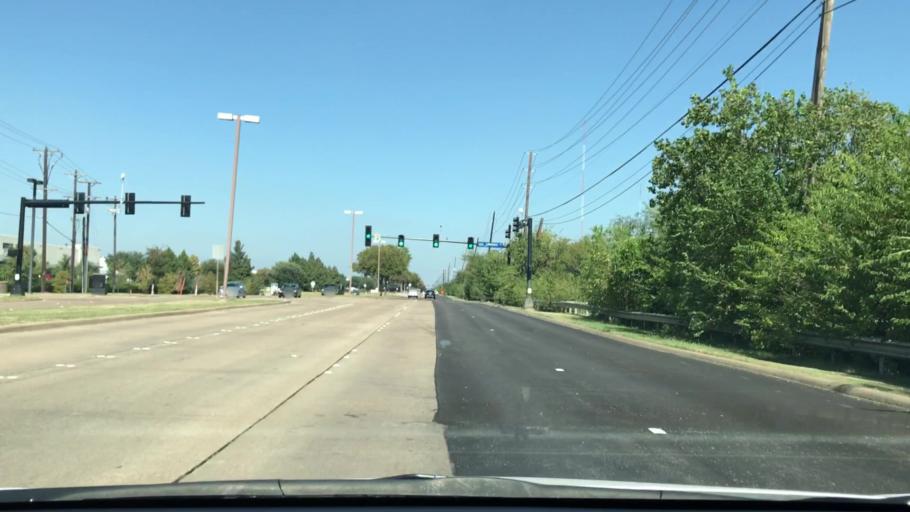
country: US
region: Texas
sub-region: Dallas County
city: Coppell
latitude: 32.9347
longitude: -96.9935
